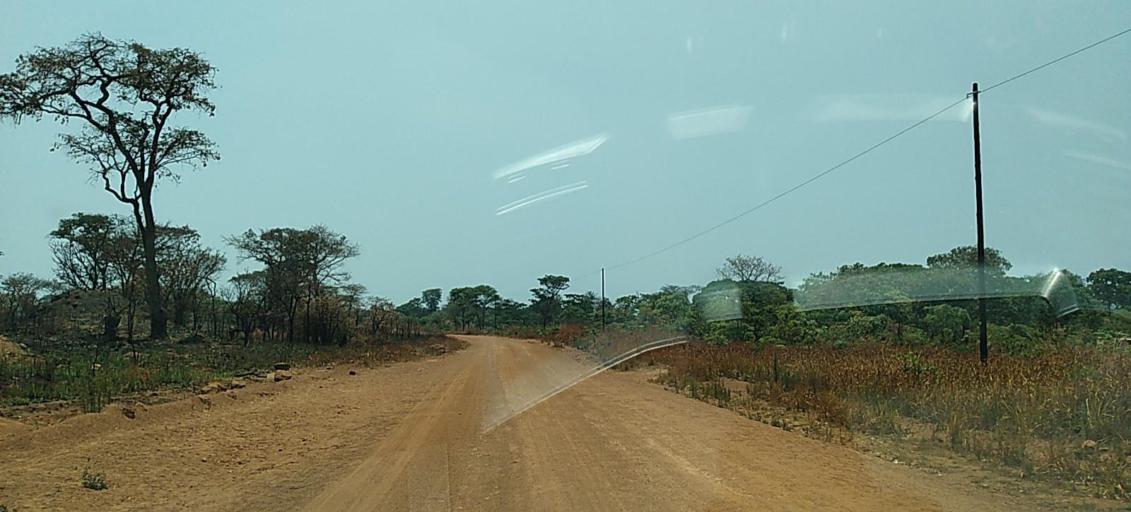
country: CD
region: Katanga
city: Kipushi
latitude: -11.9355
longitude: 26.9657
